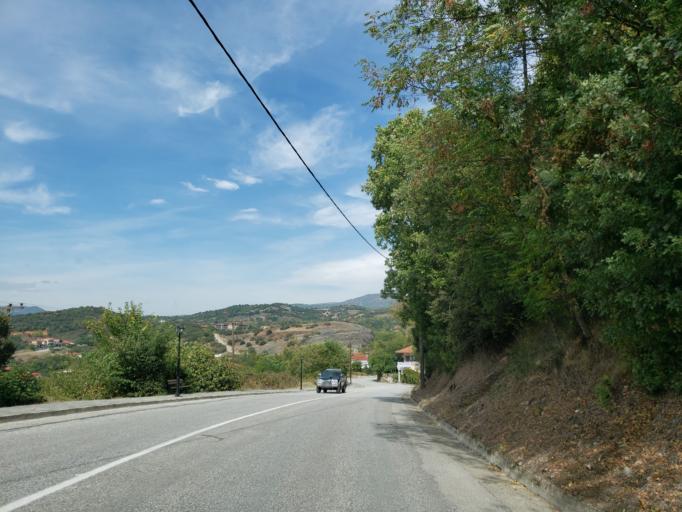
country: GR
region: Thessaly
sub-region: Trikala
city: Kastraki
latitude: 39.7111
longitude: 21.6160
